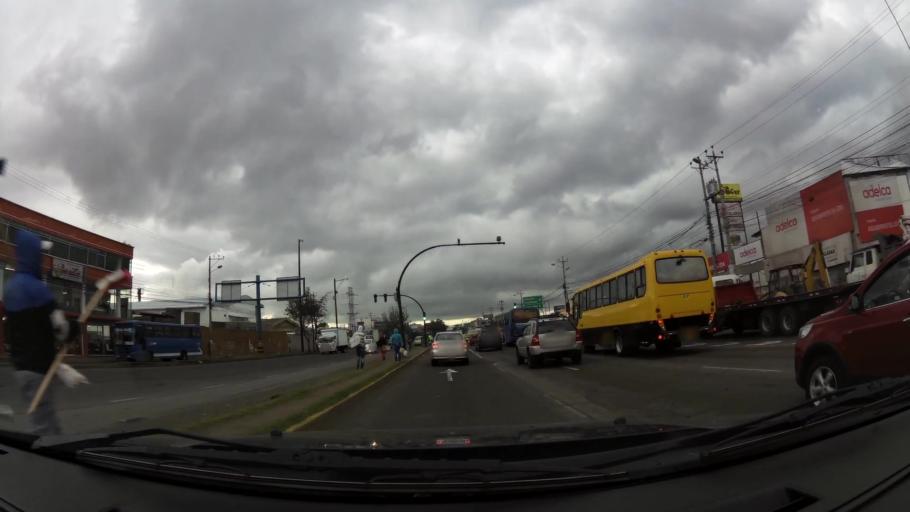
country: EC
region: Pichincha
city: Quito
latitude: -0.1075
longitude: -78.4468
